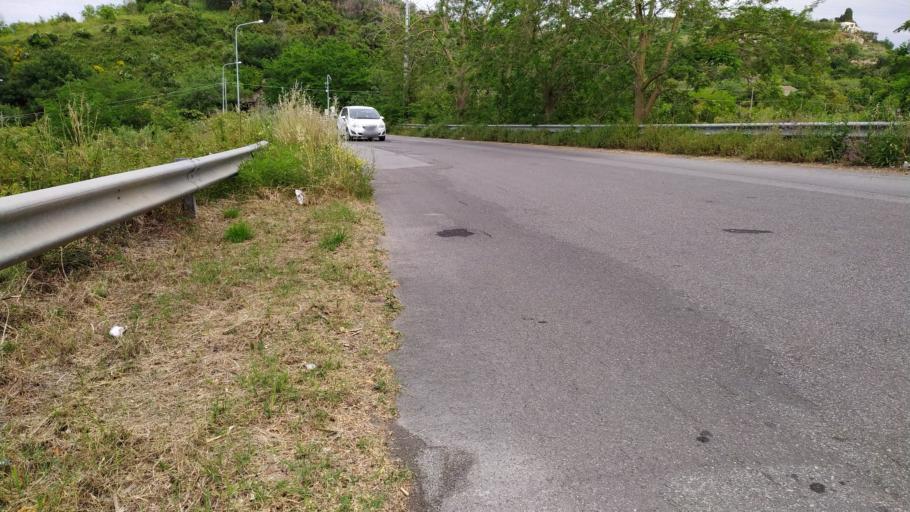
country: IT
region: Sicily
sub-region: Messina
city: San Filippo del Mela
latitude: 38.1690
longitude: 15.2810
